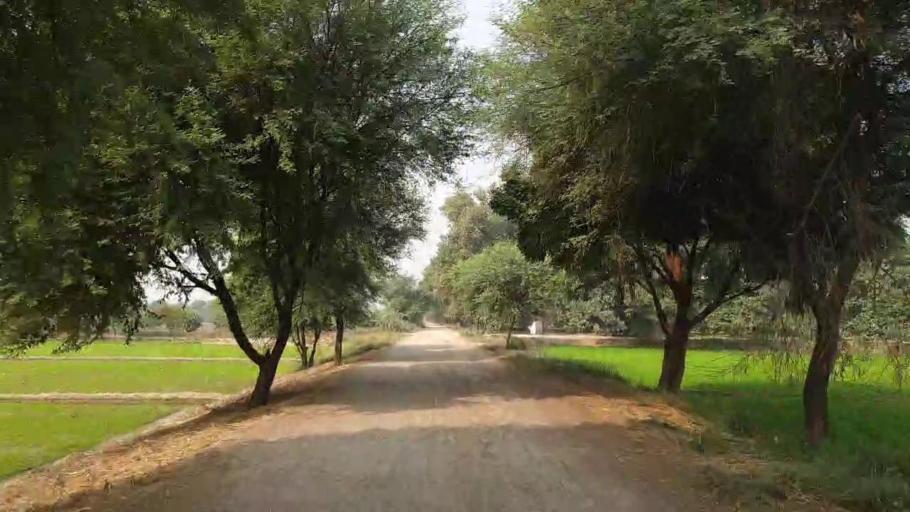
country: PK
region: Sindh
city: Tando Muhammad Khan
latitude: 25.2155
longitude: 68.5557
